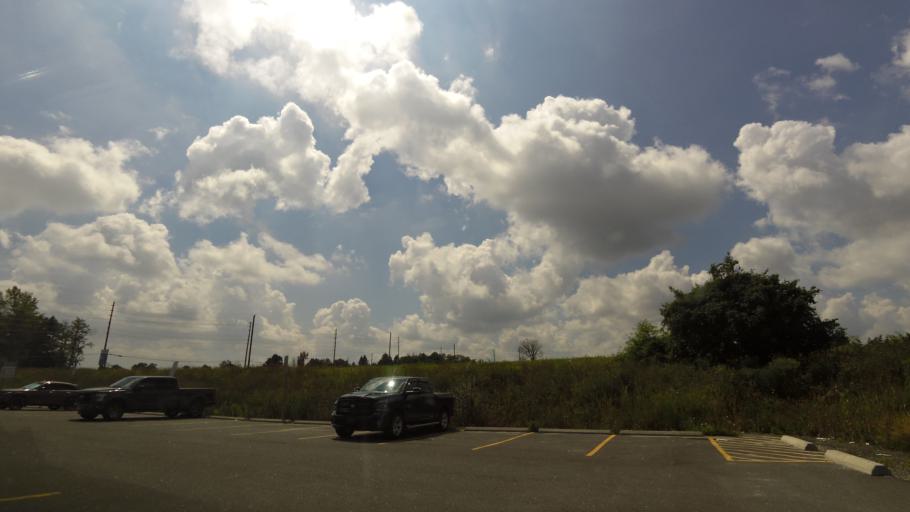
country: CA
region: Ontario
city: Ajax
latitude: 43.9425
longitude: -79.0091
